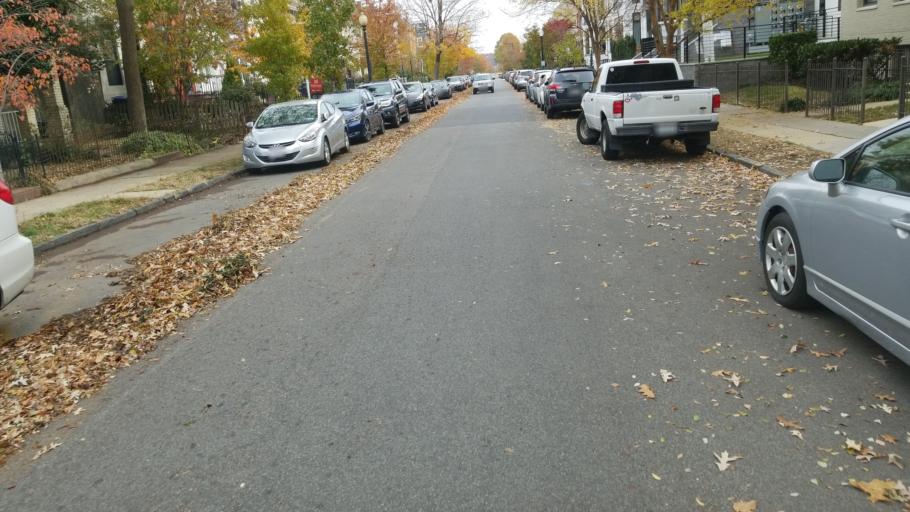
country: US
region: Washington, D.C.
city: Washington, D.C.
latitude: 38.8784
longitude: -76.9875
